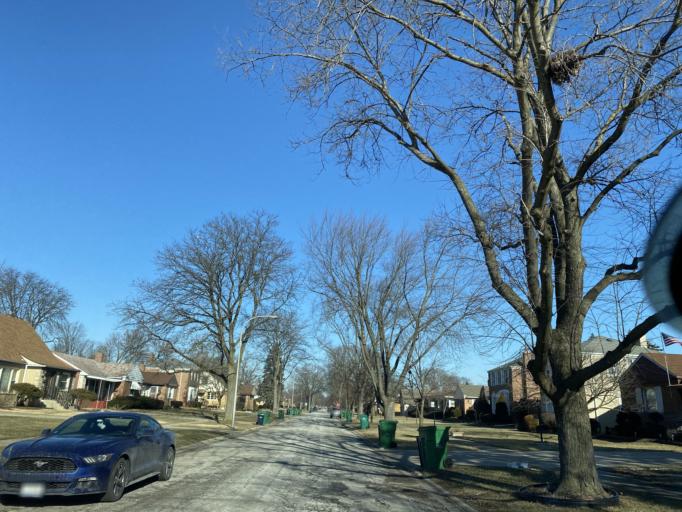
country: US
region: Illinois
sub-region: Cook County
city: Westchester
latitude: 41.8495
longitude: -87.8709
